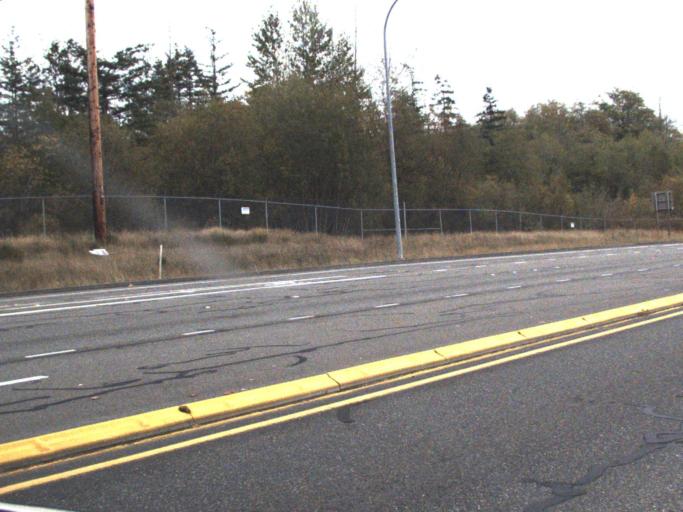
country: US
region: Washington
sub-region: Snohomish County
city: Mukilteo
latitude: 47.9096
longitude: -122.2932
